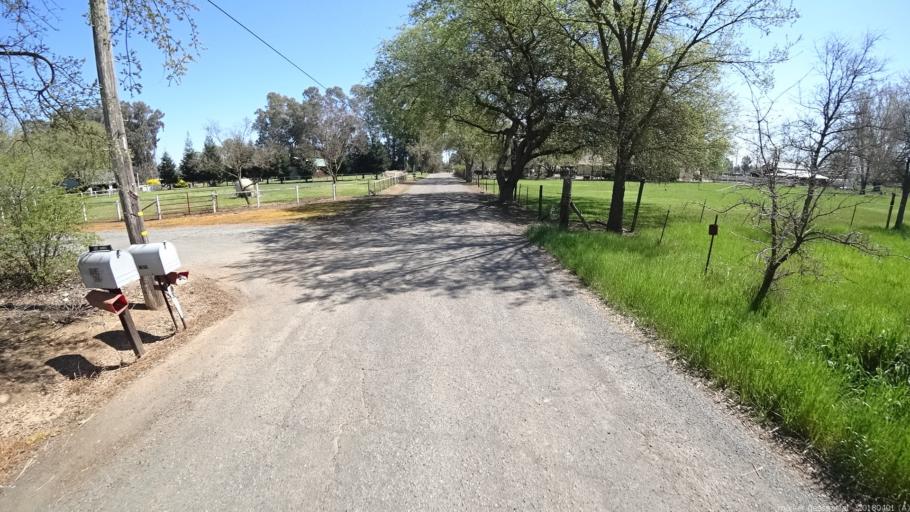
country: US
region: California
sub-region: Sacramento County
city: Rancho Murieta
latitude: 38.4474
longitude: -121.1780
